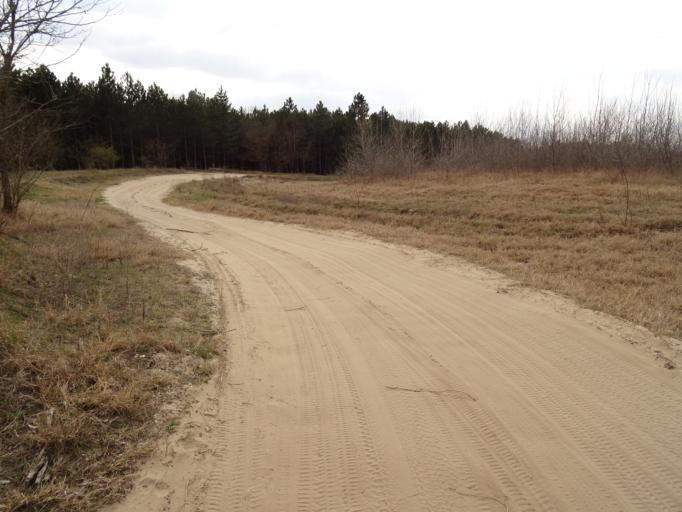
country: HU
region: Bacs-Kiskun
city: Izsak
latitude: 46.7629
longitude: 19.3285
